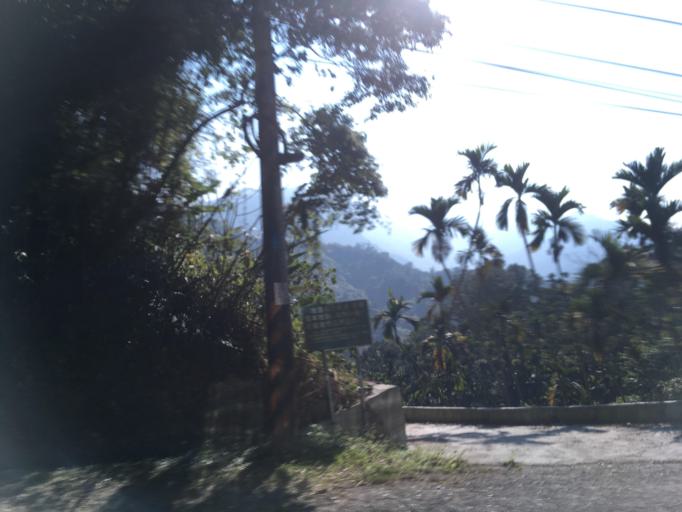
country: TW
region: Taiwan
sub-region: Chiayi
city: Jiayi Shi
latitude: 23.4346
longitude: 120.6343
